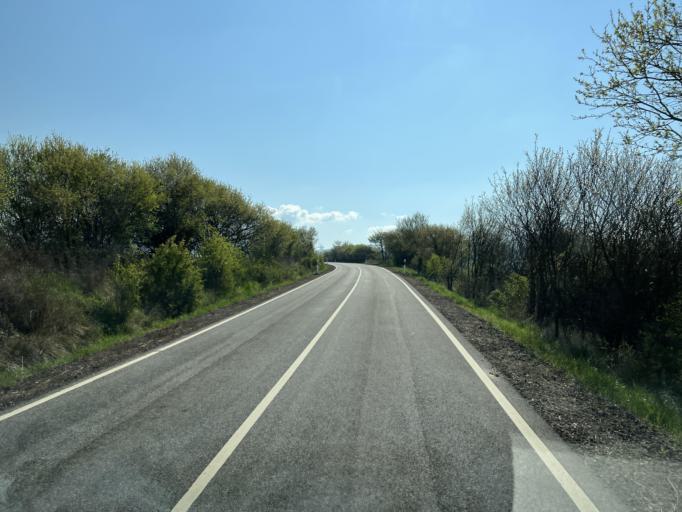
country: HU
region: Pest
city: Szob
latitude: 47.9376
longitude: 18.7910
